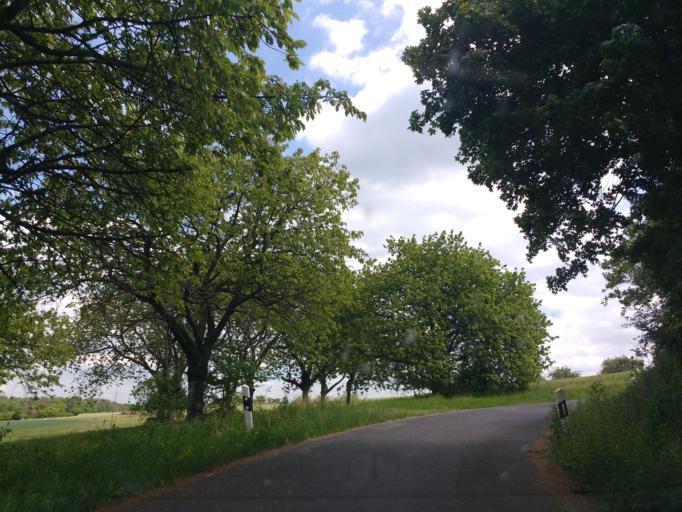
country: DE
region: Hesse
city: Witzenhausen
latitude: 51.4006
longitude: 9.8549
